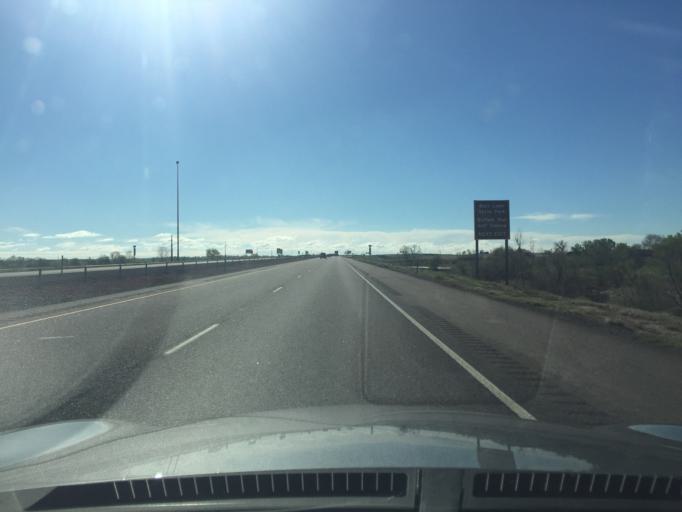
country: US
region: Colorado
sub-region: Adams County
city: Brighton
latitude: 39.9222
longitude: -104.7967
